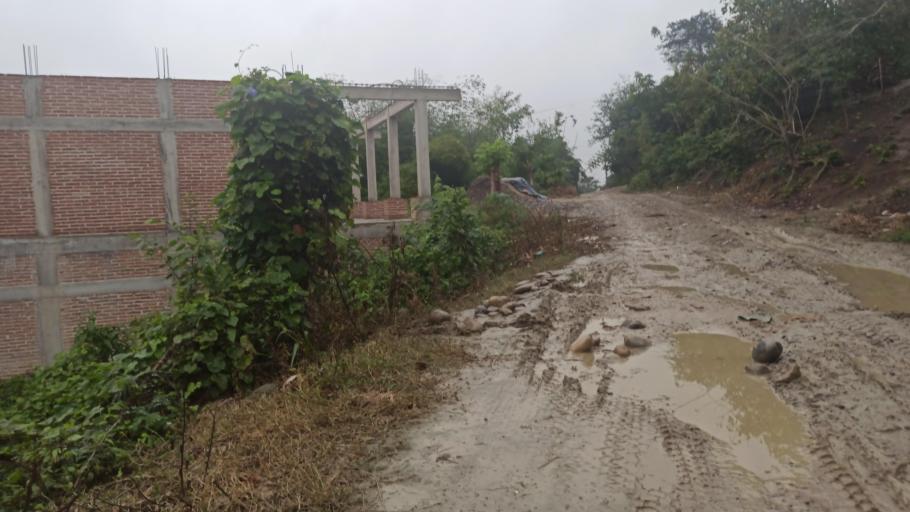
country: MX
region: Veracruz
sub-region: Papantla
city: El Chote
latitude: 20.3582
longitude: -97.3421
